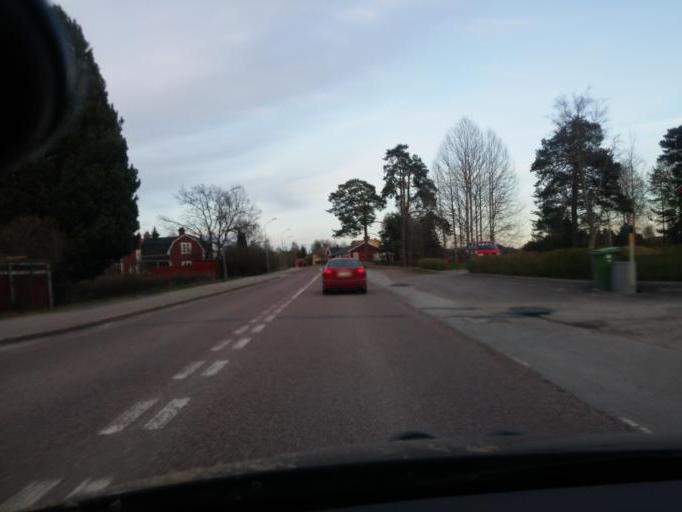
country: SE
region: Gaevleborg
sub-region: Ljusdals Kommun
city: Ljusdal
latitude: 61.8386
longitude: 16.0509
